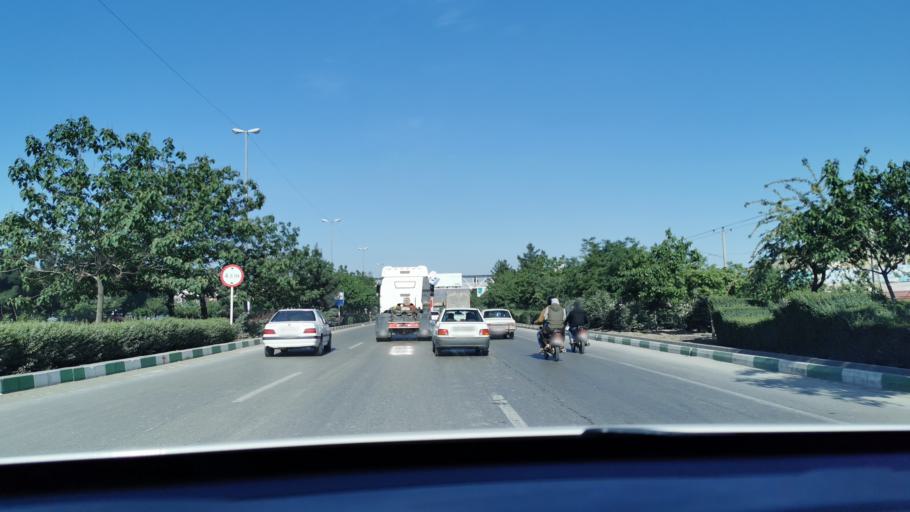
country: IR
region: Razavi Khorasan
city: Mashhad
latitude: 36.2592
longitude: 59.6409
